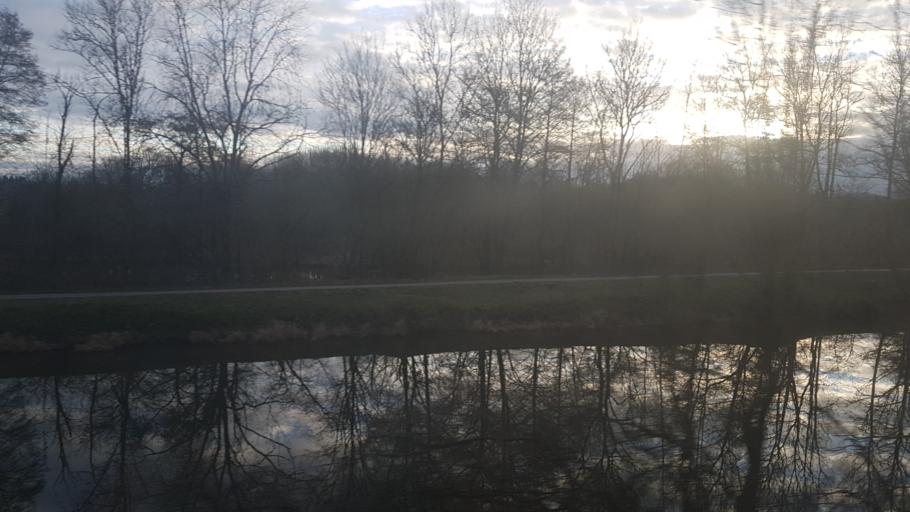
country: FR
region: Lorraine
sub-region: Departement des Vosges
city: Igney
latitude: 48.2920
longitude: 6.3973
